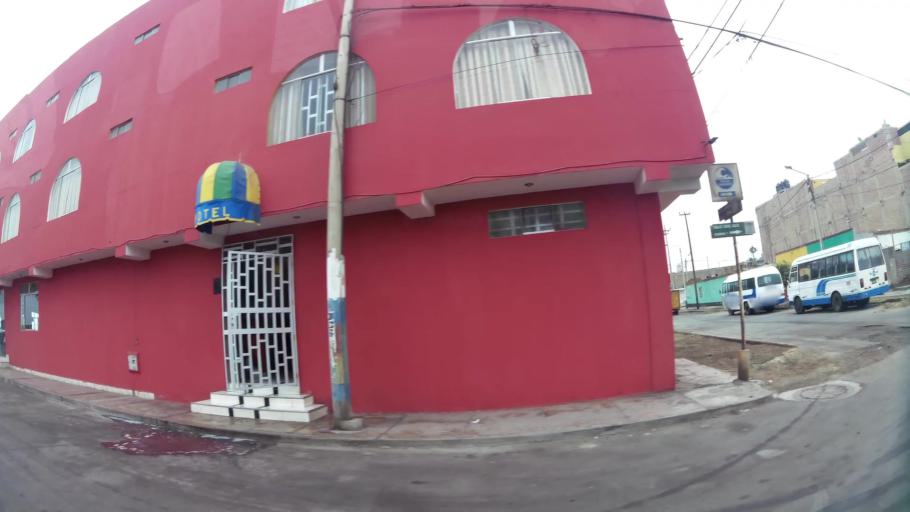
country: PE
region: Ica
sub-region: Provincia de Pisco
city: Pisco
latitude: -13.7303
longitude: -76.2230
